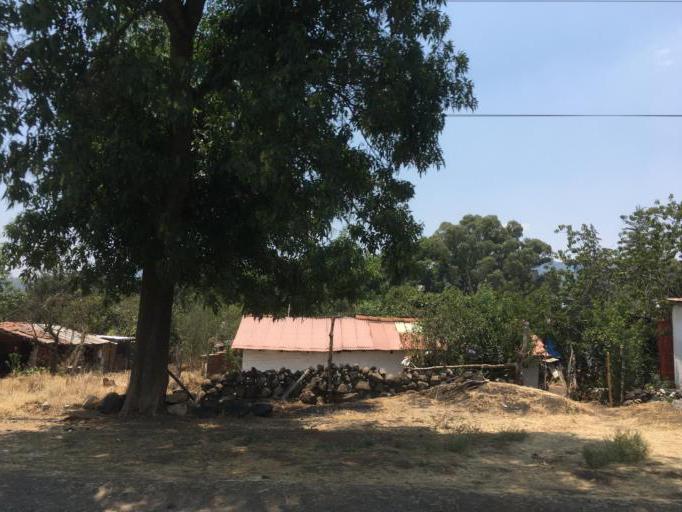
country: MX
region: Michoacan
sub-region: Morelia
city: Iratzio
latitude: 19.6311
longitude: -101.4674
